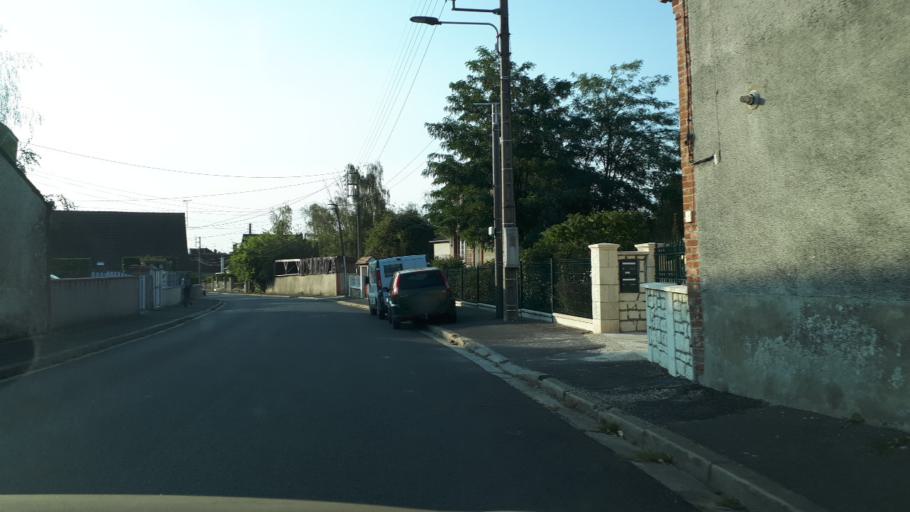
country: FR
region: Centre
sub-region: Departement du Loir-et-Cher
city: Romorantin-Lanthenay
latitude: 47.3515
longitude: 1.7521
